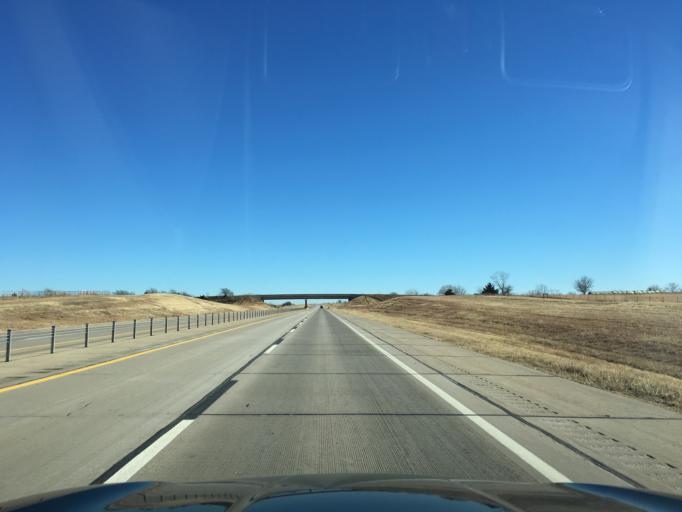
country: US
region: Oklahoma
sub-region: Noble County
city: Perry
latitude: 36.3929
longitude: -97.1969
